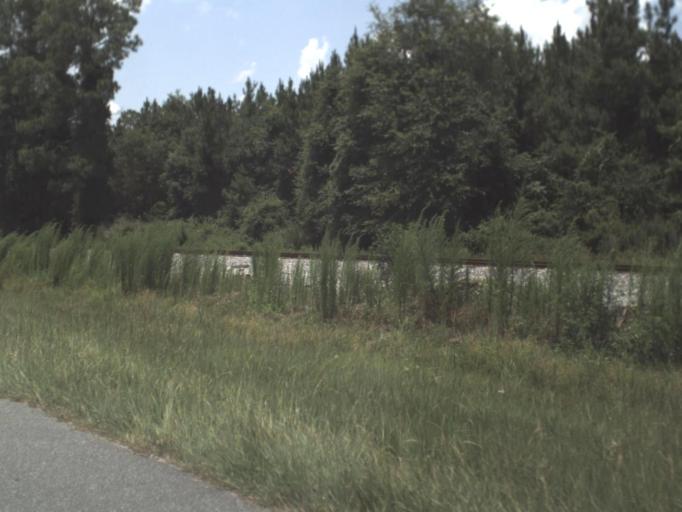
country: US
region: Florida
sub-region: Columbia County
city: Five Points
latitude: 30.2615
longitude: -82.6861
